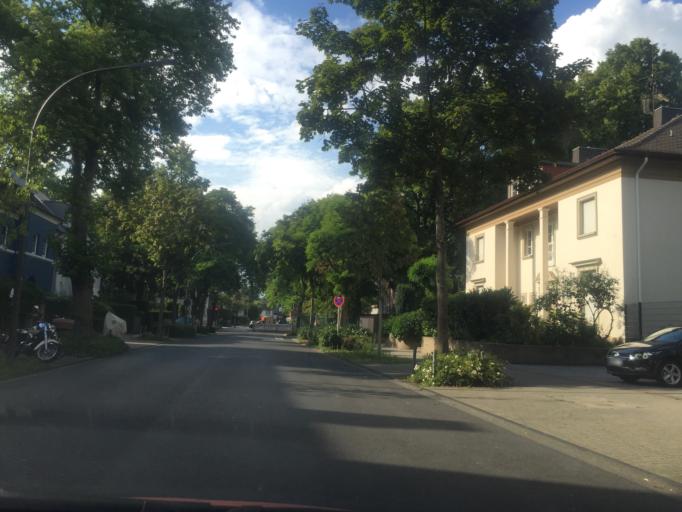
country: DE
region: North Rhine-Westphalia
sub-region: Regierungsbezirk Koln
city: Bayenthal
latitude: 50.9037
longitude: 6.9720
